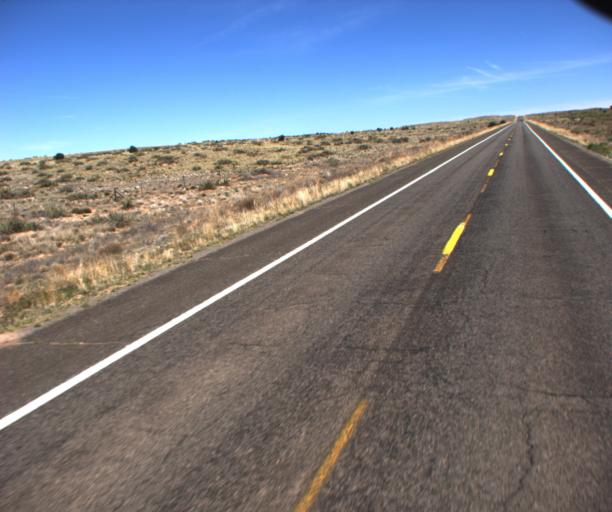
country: US
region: Arizona
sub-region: Mohave County
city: Peach Springs
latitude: 35.5092
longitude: -113.5130
